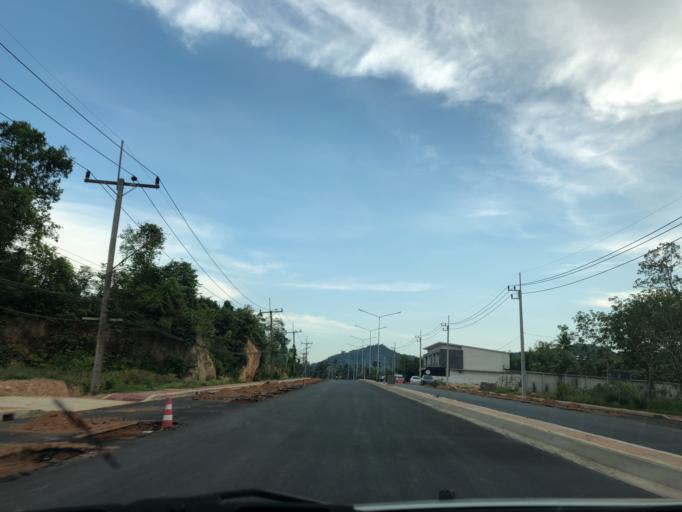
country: TH
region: Phangnga
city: Ban Ao Nang
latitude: 8.0644
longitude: 98.8431
